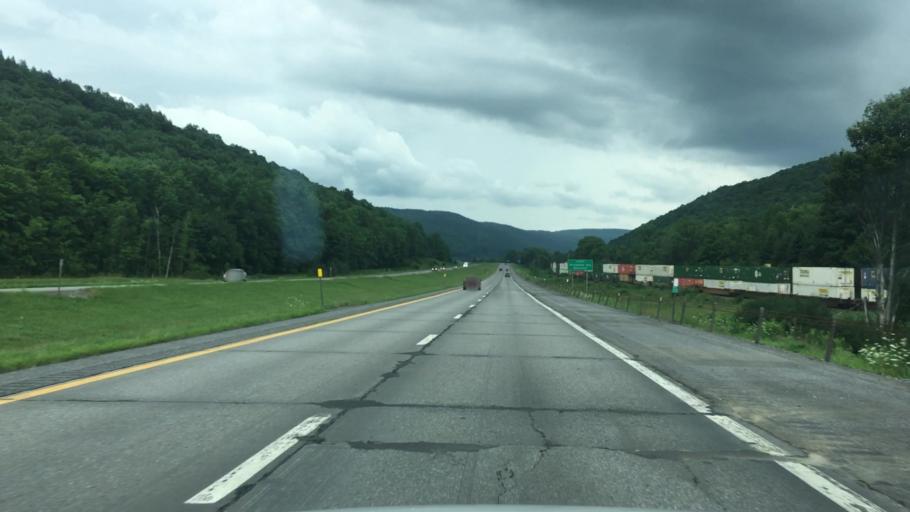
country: US
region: New York
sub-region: Otsego County
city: Worcester
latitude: 42.6398
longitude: -74.6517
